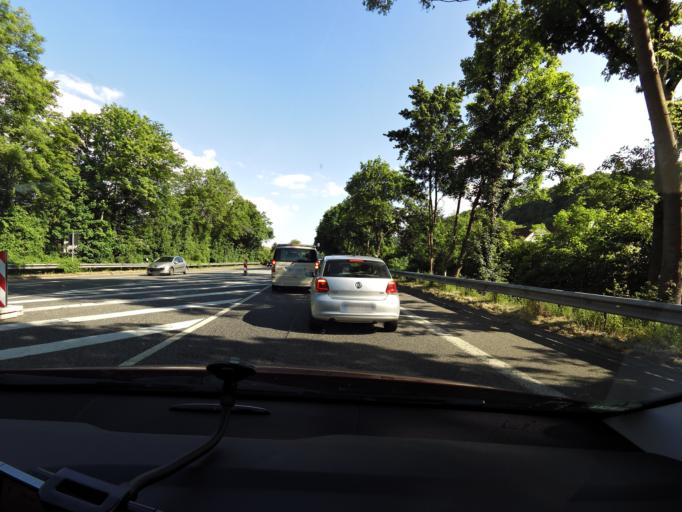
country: DE
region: Rheinland-Pfalz
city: Bad Breisig
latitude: 50.5187
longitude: 7.2898
